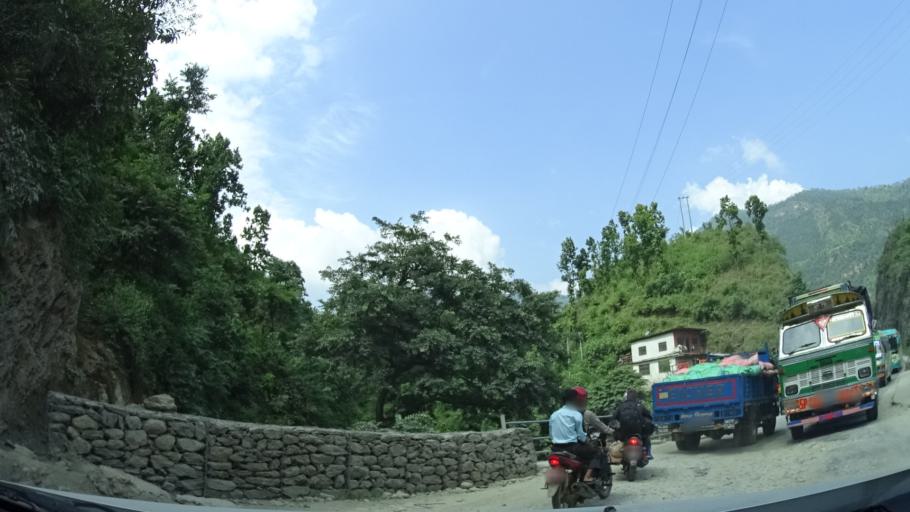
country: NP
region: Central Region
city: Kirtipur
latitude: 27.8064
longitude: 84.9684
